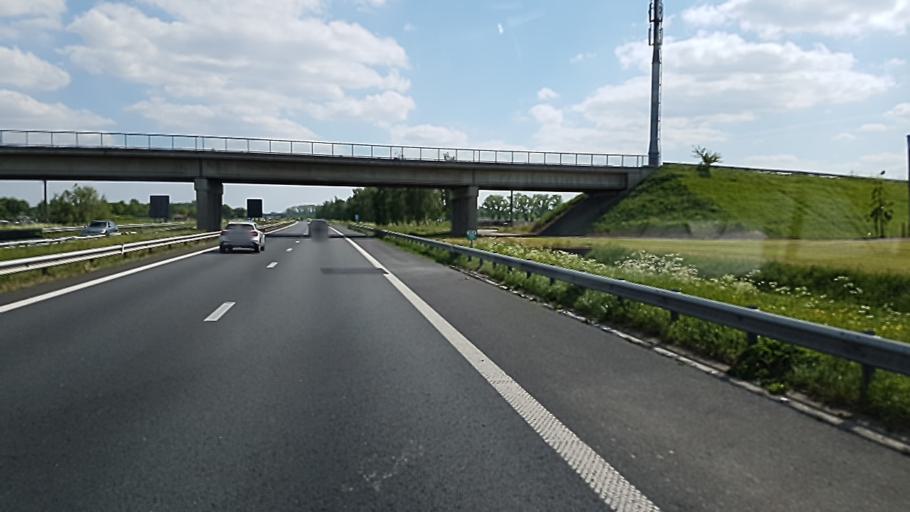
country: BE
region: Flanders
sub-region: Provincie West-Vlaanderen
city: Lichtervelde
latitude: 51.0687
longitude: 3.1540
